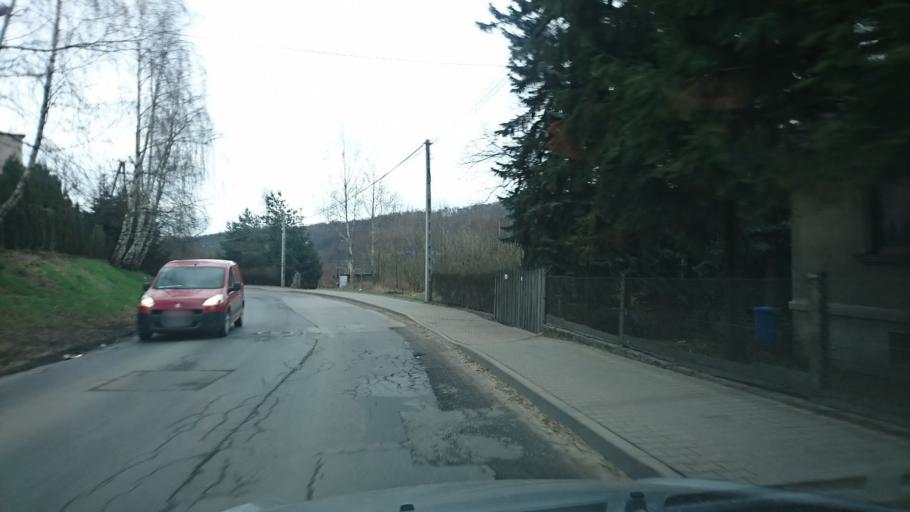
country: PL
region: Lesser Poland Voivodeship
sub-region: Powiat wielicki
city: Wieliczka
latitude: 50.0037
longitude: 20.0071
